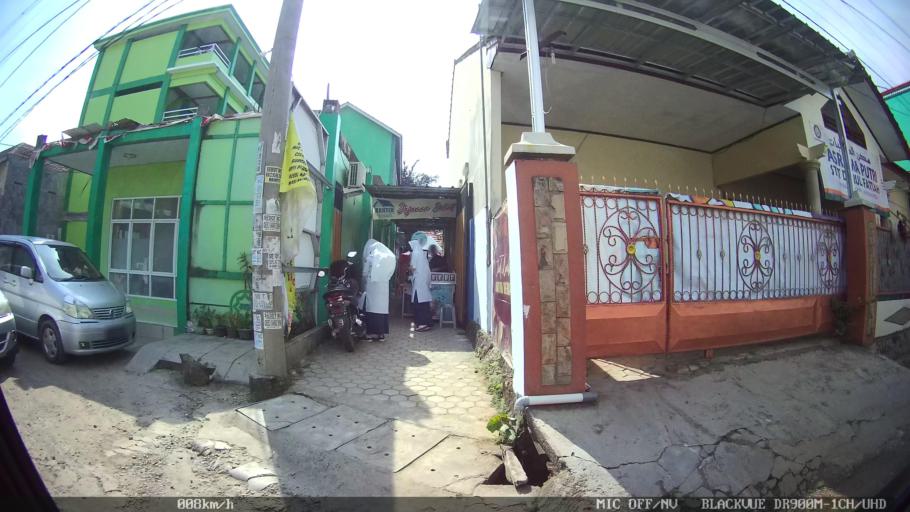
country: ID
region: Lampung
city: Kedaton
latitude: -5.3734
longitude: 105.2385
